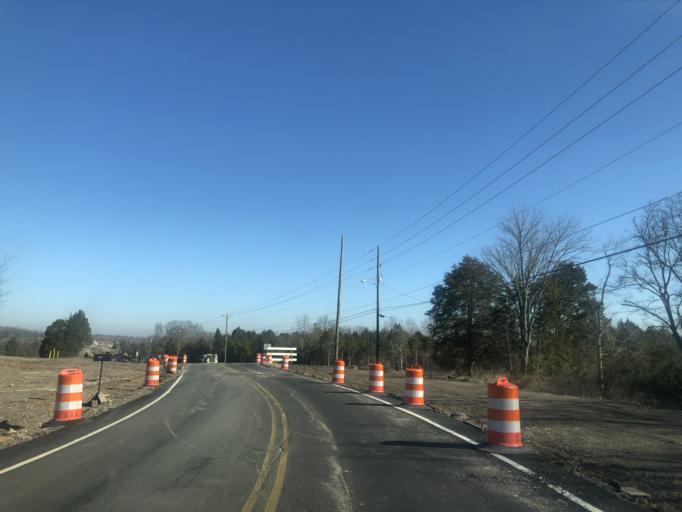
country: US
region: Tennessee
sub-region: Rutherford County
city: Smyrna
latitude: 35.9547
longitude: -86.5471
